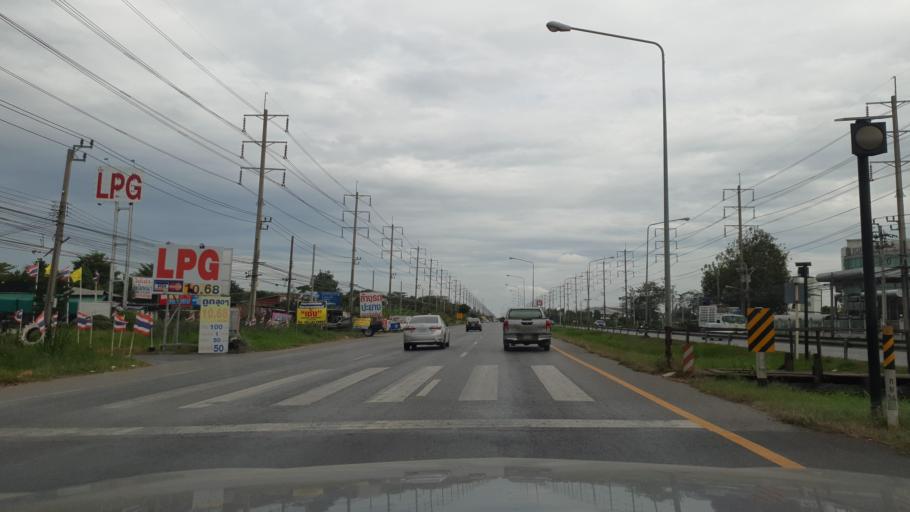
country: TH
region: Bangkok
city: Nong Chok
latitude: 13.8097
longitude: 100.8116
